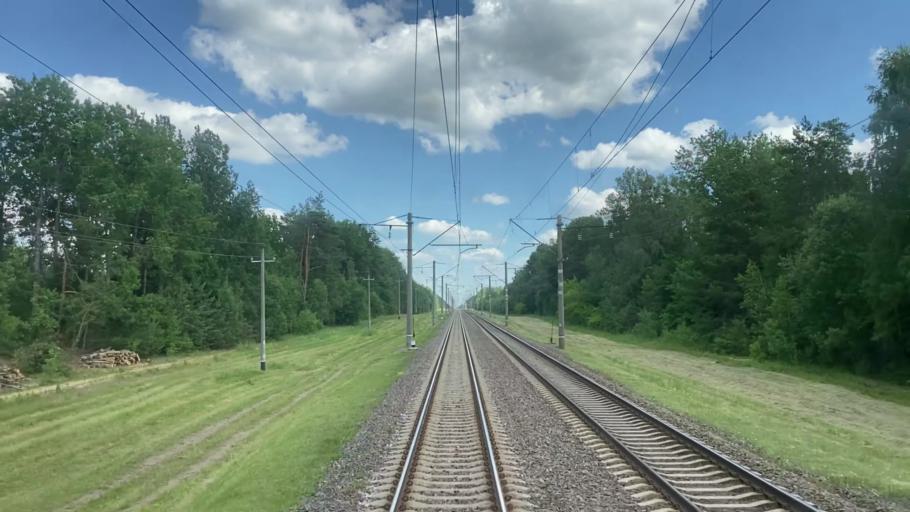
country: BY
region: Brest
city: Ivatsevichy
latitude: 52.7374
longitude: 25.3693
